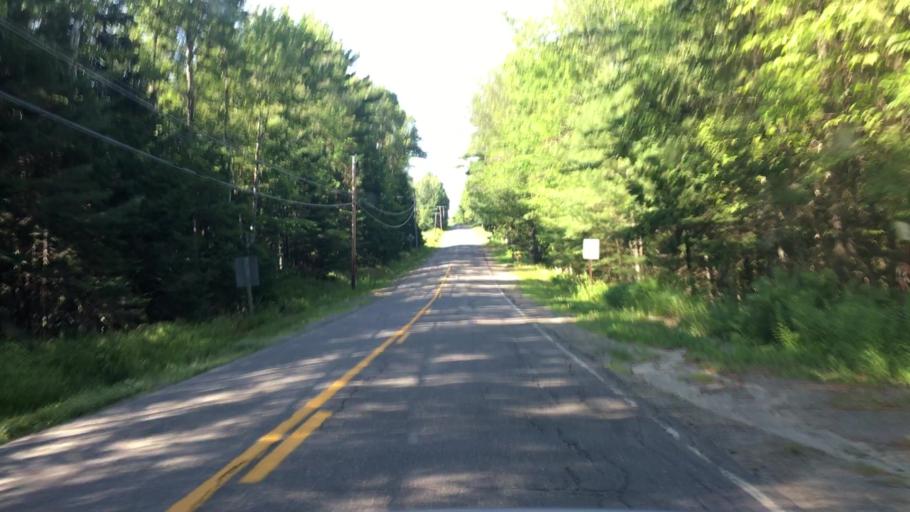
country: US
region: Maine
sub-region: Penobscot County
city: Enfield
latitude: 45.2600
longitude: -68.5632
